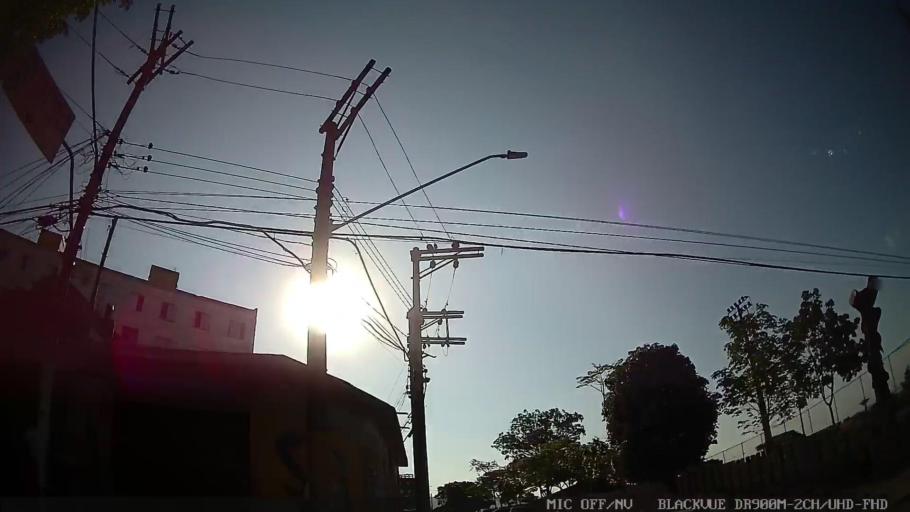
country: BR
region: Sao Paulo
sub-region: Ferraz De Vasconcelos
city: Ferraz de Vasconcelos
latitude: -23.5474
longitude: -46.4358
